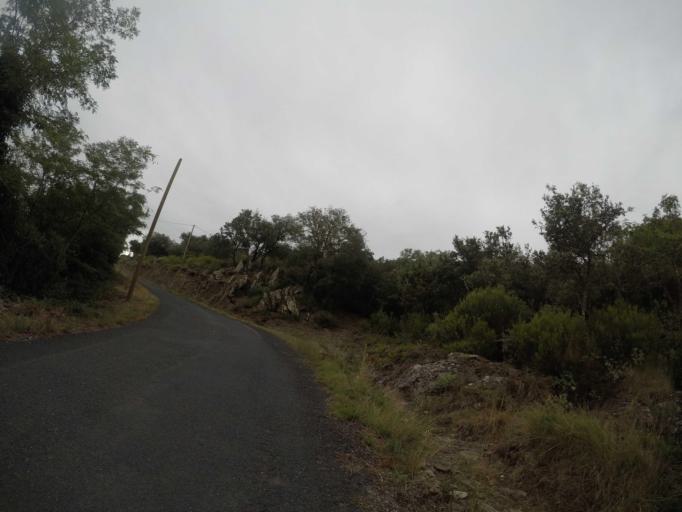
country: FR
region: Languedoc-Roussillon
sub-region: Departement des Pyrenees-Orientales
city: Ille-sur-Tet
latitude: 42.6225
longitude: 2.6191
